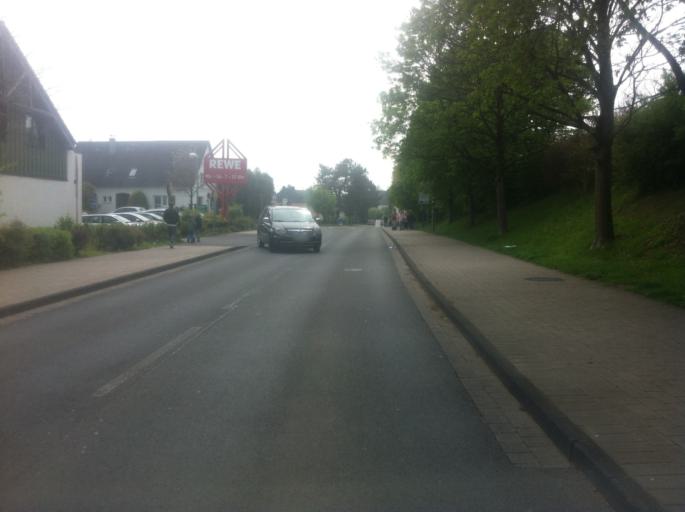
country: DE
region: North Rhine-Westphalia
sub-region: Regierungsbezirk Koln
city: Hennef
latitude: 50.8460
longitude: 7.3402
